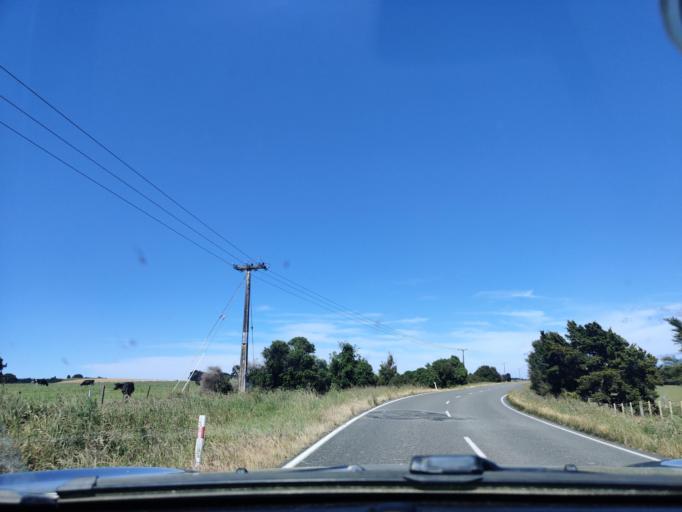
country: NZ
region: Wellington
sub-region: Upper Hutt City
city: Upper Hutt
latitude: -41.3264
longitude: 175.2433
